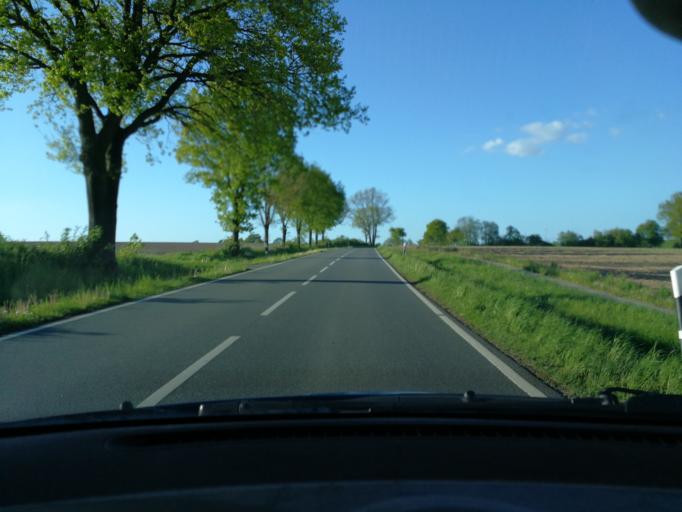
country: DE
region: Lower Saxony
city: Betzendorf
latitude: 53.1283
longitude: 10.3078
